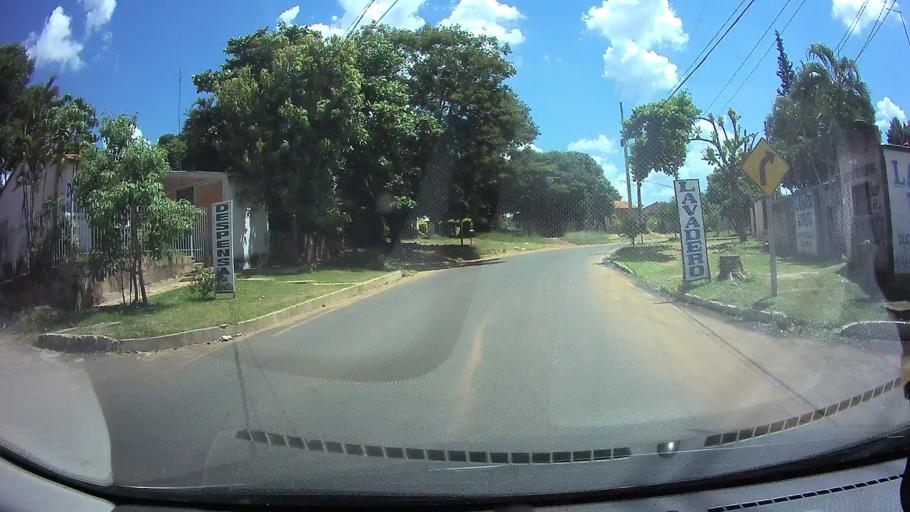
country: PY
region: Central
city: Limpio
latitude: -25.1676
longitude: -57.4418
